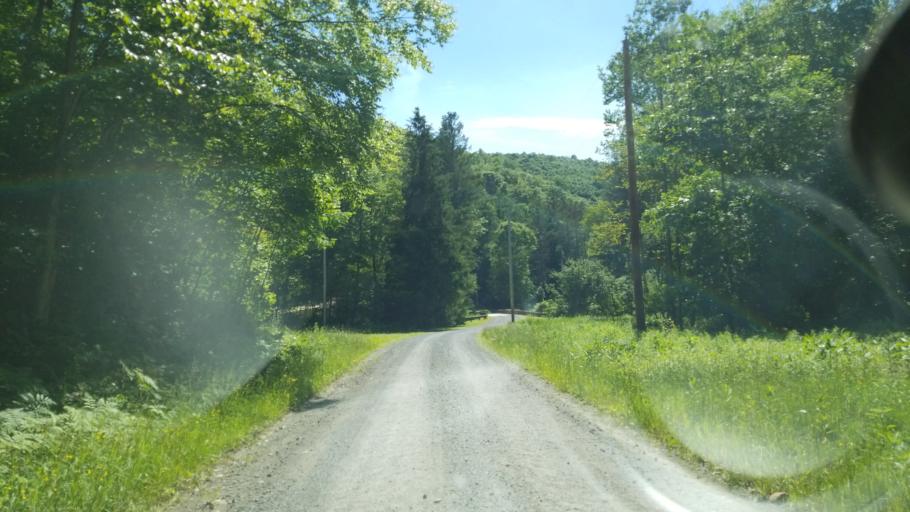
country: US
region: Pennsylvania
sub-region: Clearfield County
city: Clearfield
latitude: 41.2207
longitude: -78.3905
